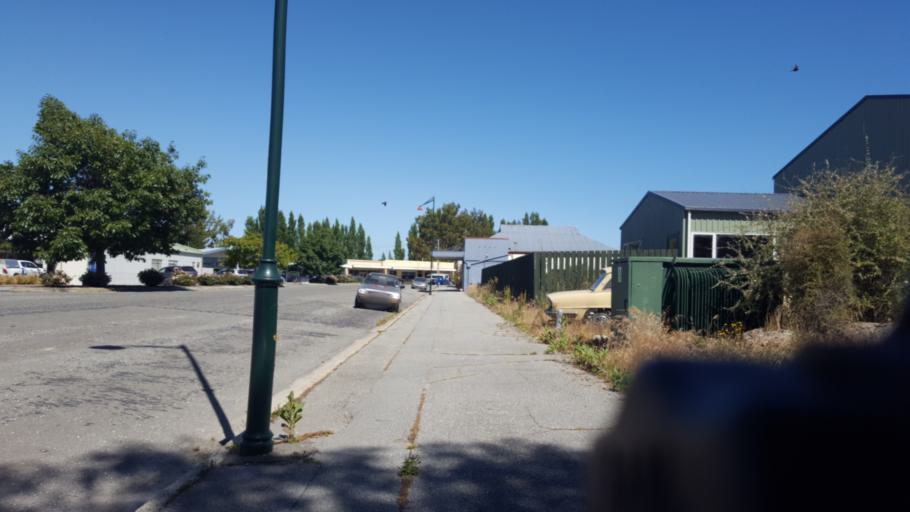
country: NZ
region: Otago
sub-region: Dunedin City
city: Dunedin
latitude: -45.1290
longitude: 170.0999
